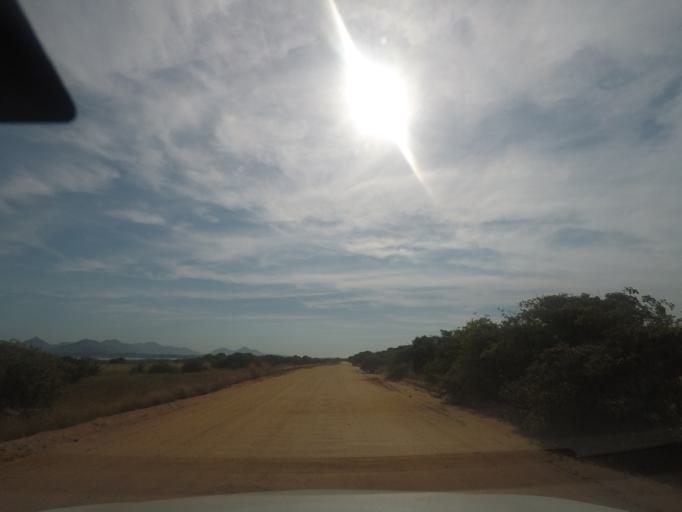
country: BR
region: Rio de Janeiro
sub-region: Marica
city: Marica
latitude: -22.9599
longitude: -42.8678
